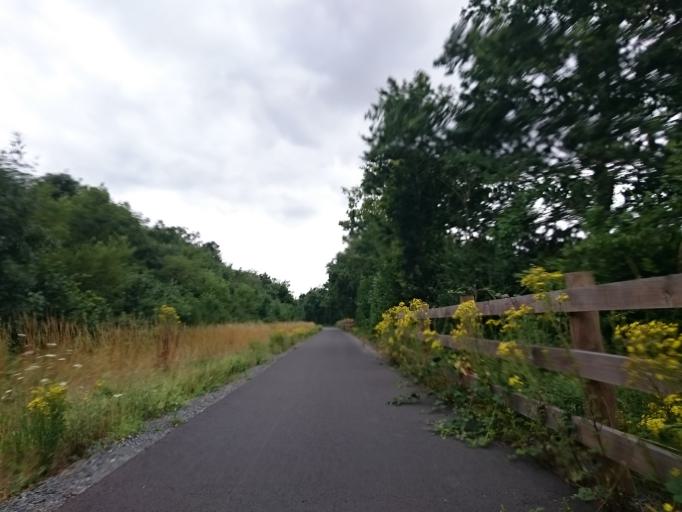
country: FR
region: Lower Normandy
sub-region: Departement du Calvados
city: Bully
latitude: 49.0914
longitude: -0.4193
